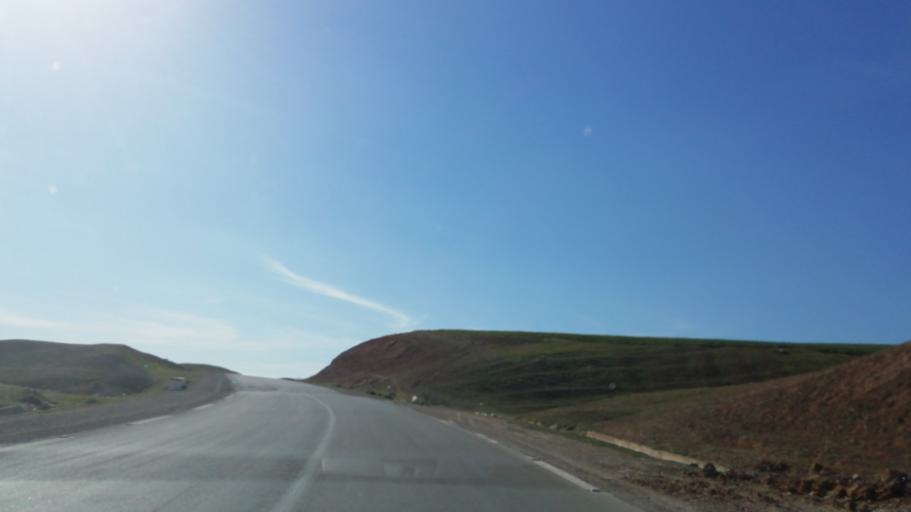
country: DZ
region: Mascara
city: Oued el Abtal
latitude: 35.4495
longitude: 0.8108
